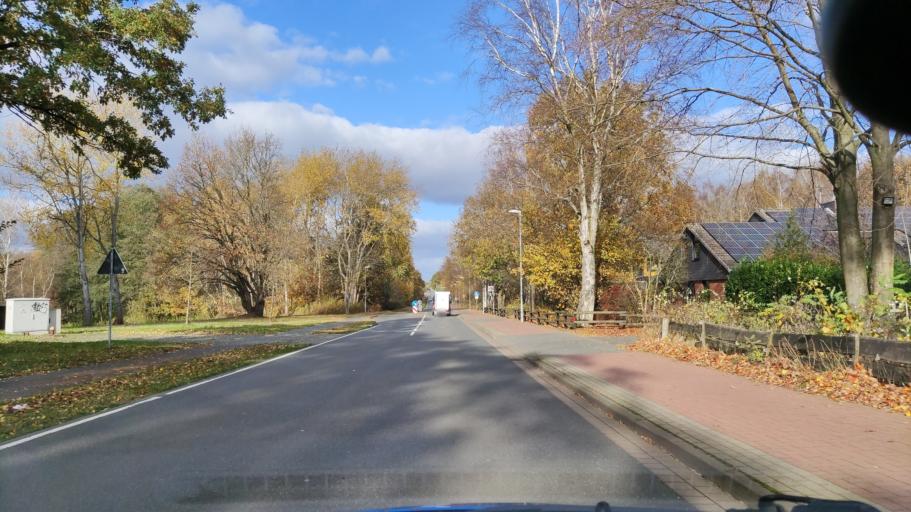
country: DE
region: Lower Saxony
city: Munster
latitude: 52.9966
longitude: 10.0899
